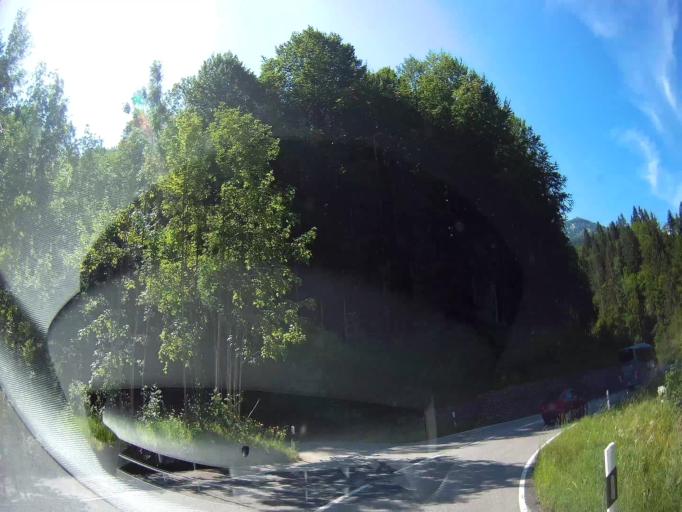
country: DE
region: Bavaria
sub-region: Upper Bavaria
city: Berchtesgaden
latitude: 47.6337
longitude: 13.0600
